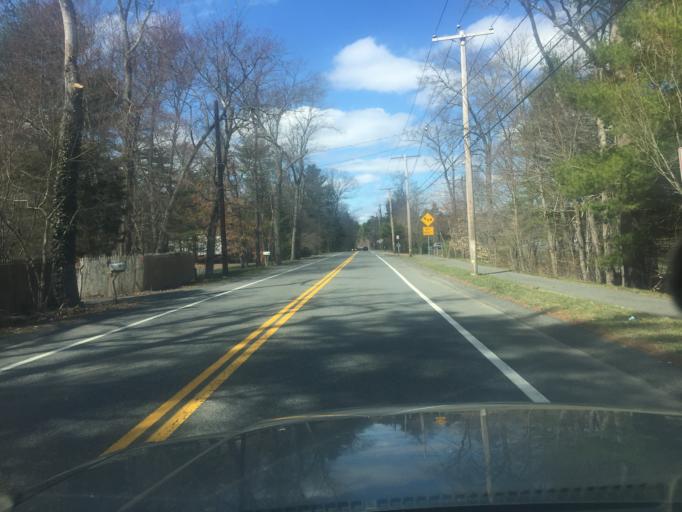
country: US
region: Massachusetts
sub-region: Norfolk County
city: Norfolk
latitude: 42.1019
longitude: -71.3073
